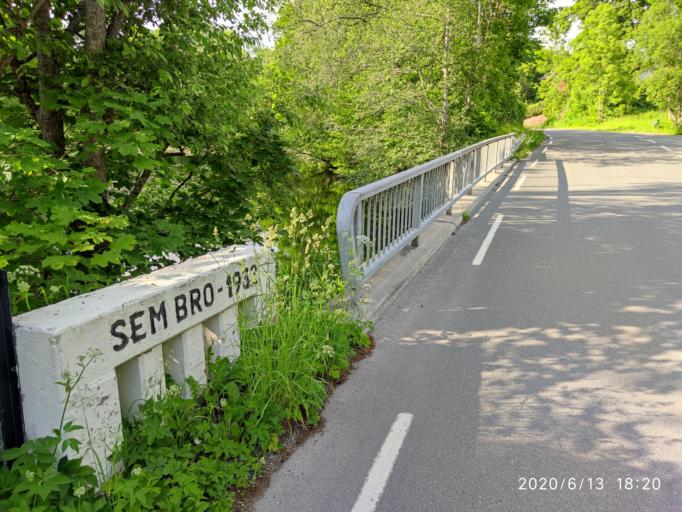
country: NO
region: Akershus
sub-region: Asker
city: Asker
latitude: 59.8516
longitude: 10.4216
